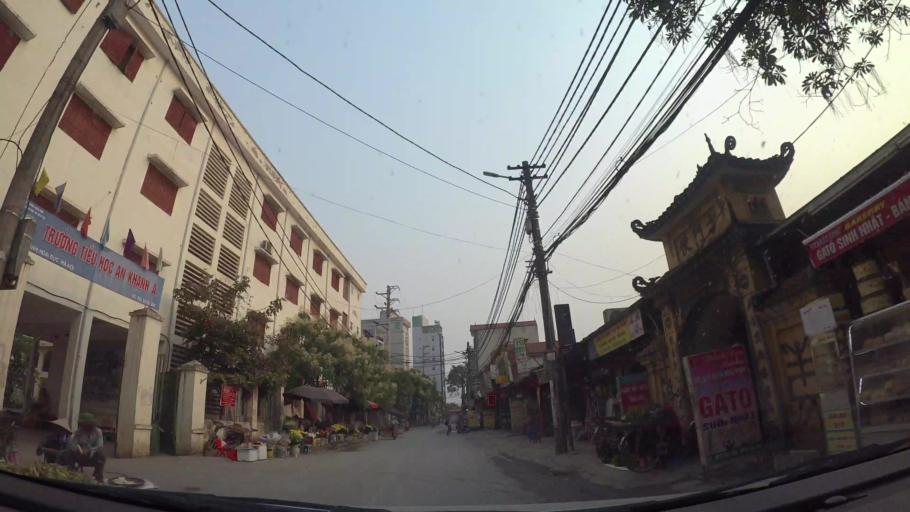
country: VN
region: Ha Noi
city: Cau Dien
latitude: 21.0064
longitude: 105.7202
